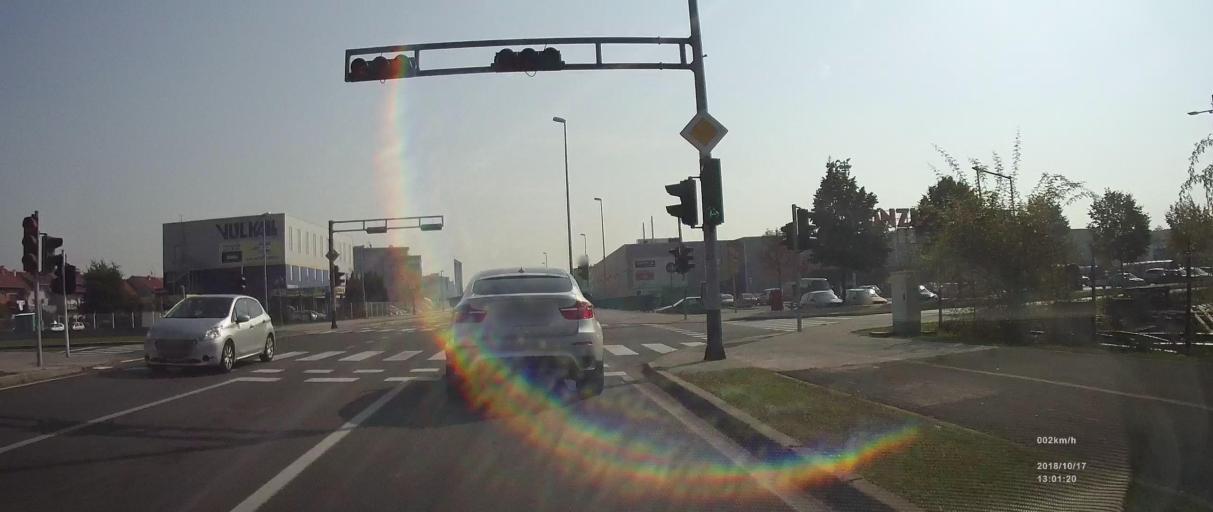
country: HR
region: Zagrebacka
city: Gradici
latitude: 45.7126
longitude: 16.0584
